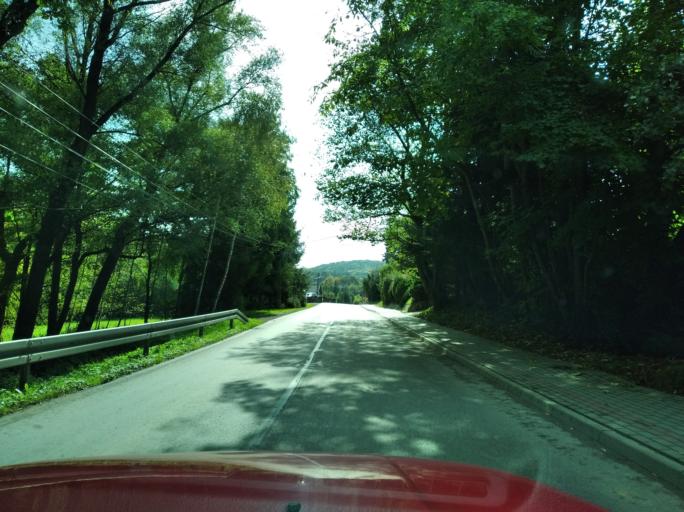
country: PL
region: Subcarpathian Voivodeship
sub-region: Powiat rzeszowski
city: Tyczyn
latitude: 49.9438
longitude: 22.0214
